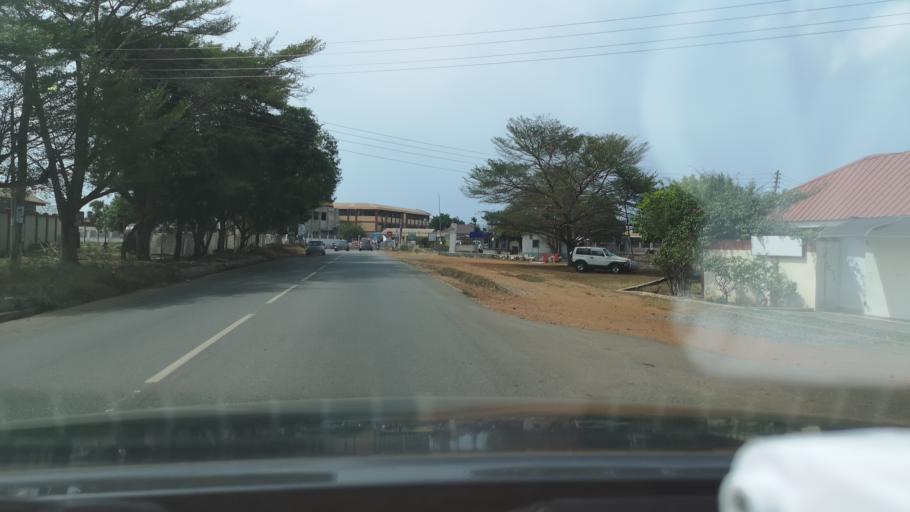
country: GH
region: Greater Accra
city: Tema
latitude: 5.6692
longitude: -0.0275
